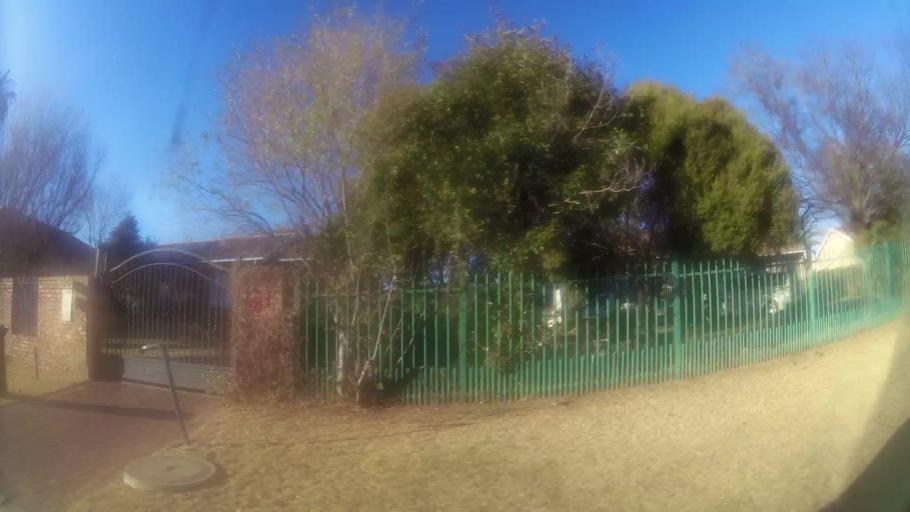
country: ZA
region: Gauteng
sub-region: City of Tshwane Metropolitan Municipality
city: Centurion
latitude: -25.9055
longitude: 28.1291
